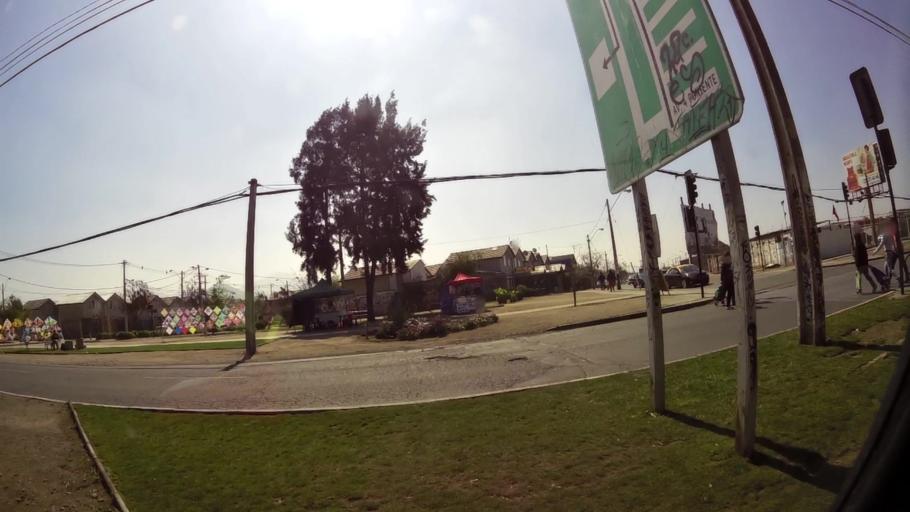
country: CL
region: Santiago Metropolitan
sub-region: Provincia de Santiago
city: Lo Prado
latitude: -33.5056
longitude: -70.7916
